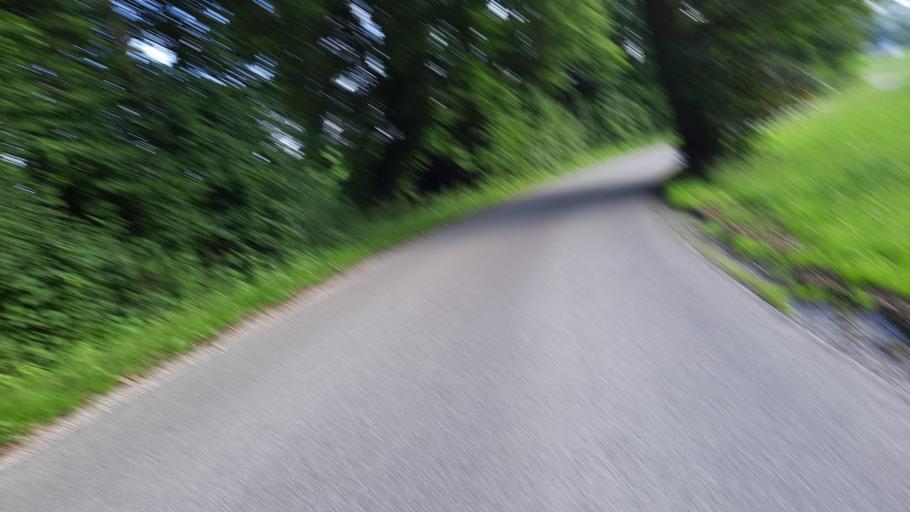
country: DE
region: Bavaria
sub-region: Upper Bavaria
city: Glonn
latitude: 47.9631
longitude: 11.9005
